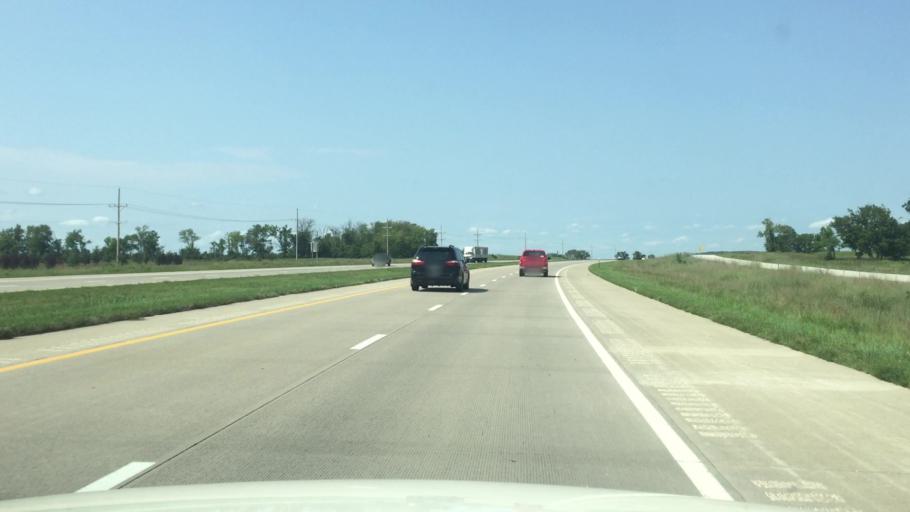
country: US
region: Kansas
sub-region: Linn County
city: Pleasanton
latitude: 38.2081
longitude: -94.7050
